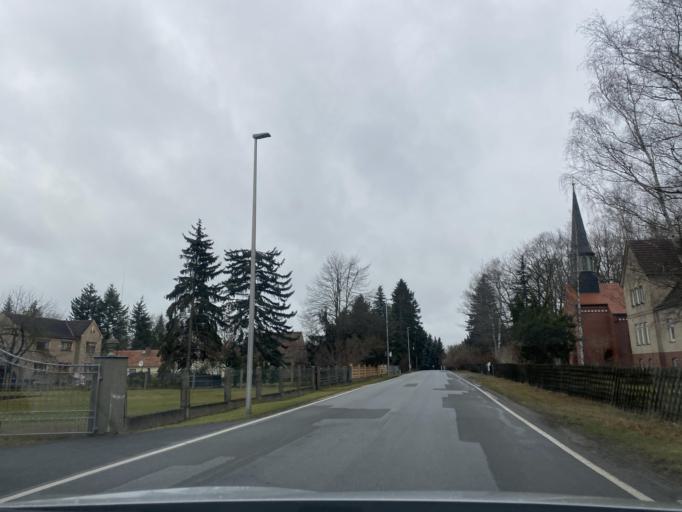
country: DE
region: Saxony
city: Rothenburg
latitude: 51.3276
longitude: 14.9731
